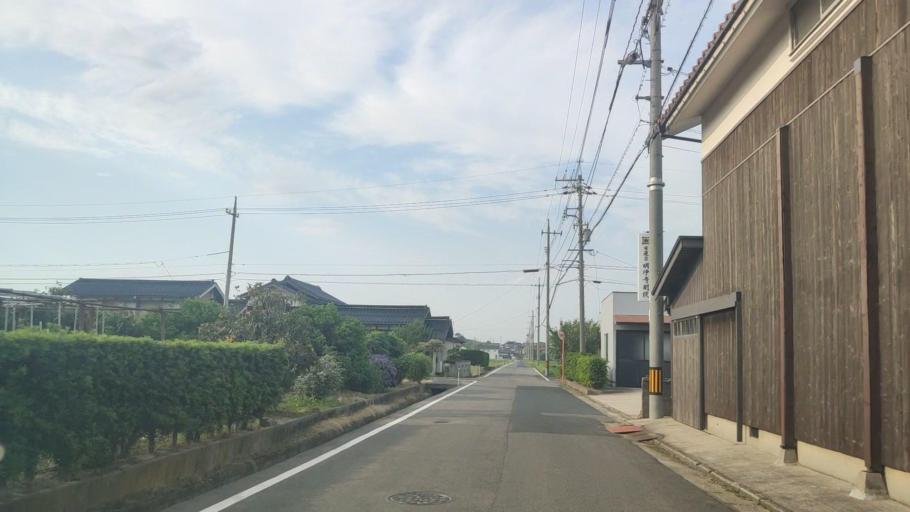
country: JP
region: Tottori
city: Kurayoshi
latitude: 35.4838
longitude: 133.8128
